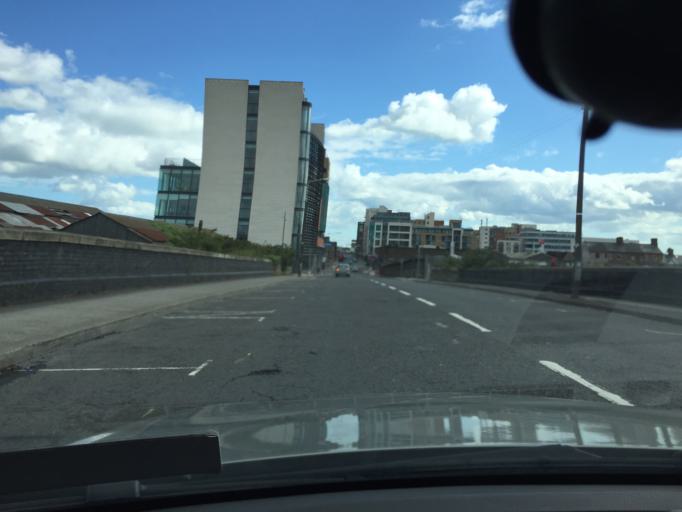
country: IE
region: Leinster
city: Ringsend
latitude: 53.3504
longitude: -6.2375
